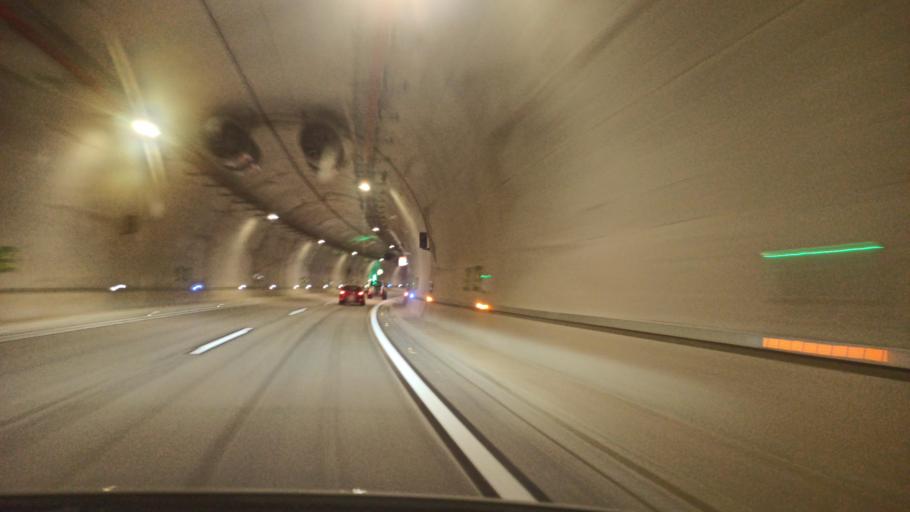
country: ES
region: Catalonia
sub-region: Provincia de Barcelona
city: Vallirana
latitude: 41.3817
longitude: 1.9338
